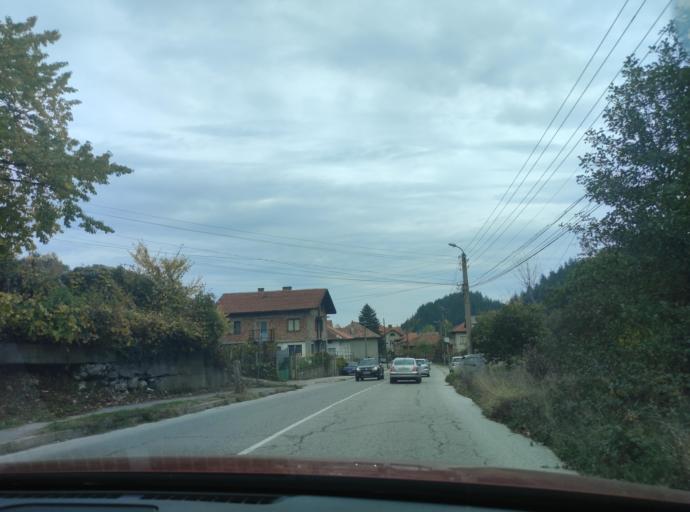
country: BG
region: Montana
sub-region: Obshtina Berkovitsa
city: Berkovitsa
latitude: 43.1937
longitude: 23.1604
